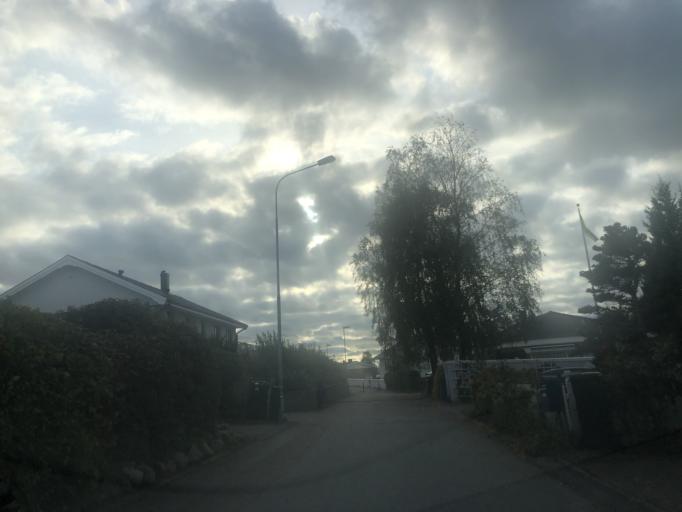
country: SE
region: Vaestra Goetaland
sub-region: Goteborg
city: Majorna
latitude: 57.6371
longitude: 11.9469
